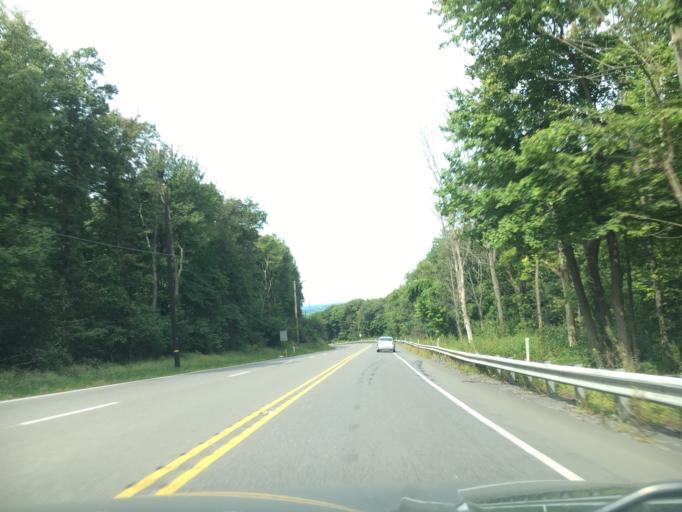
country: US
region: Pennsylvania
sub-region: Carbon County
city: Summit Hill
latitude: 40.7076
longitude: -75.8146
